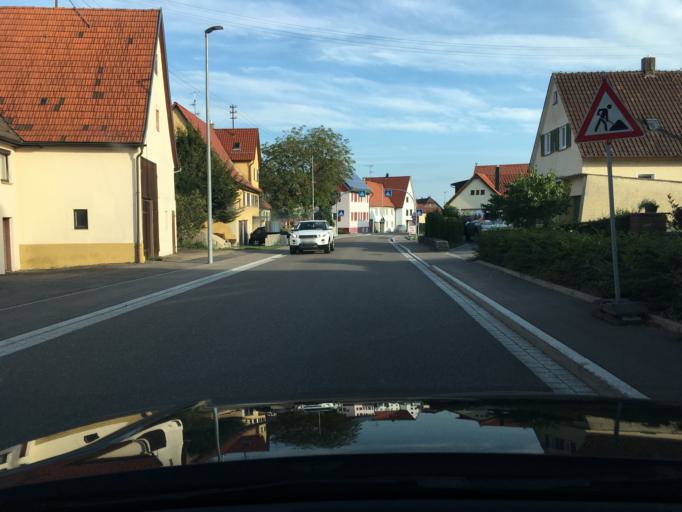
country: DE
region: Baden-Wuerttemberg
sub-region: Regierungsbezirk Stuttgart
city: Schorndorf
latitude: 48.7766
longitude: 9.5529
